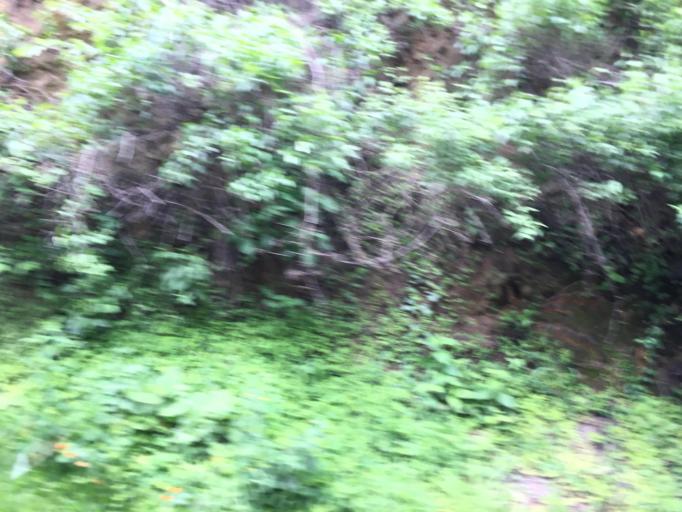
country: GT
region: Sacatepequez
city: Pastores
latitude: 14.5891
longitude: -90.7511
